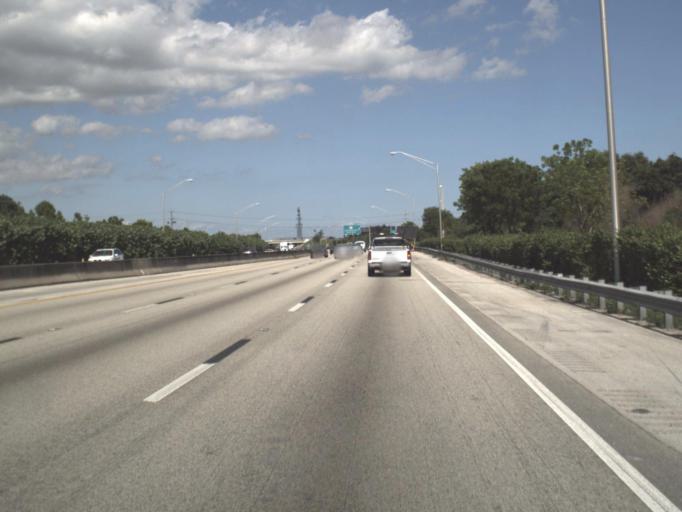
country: US
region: Florida
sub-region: Broward County
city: Pembroke Pines
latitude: 26.0003
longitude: -80.2190
